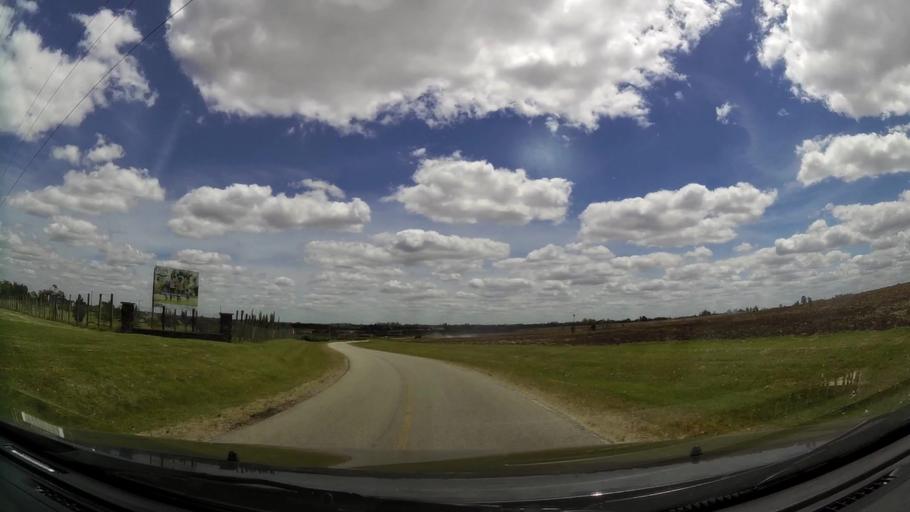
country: UY
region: Canelones
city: Colonia Nicolich
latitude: -34.7934
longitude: -56.0147
